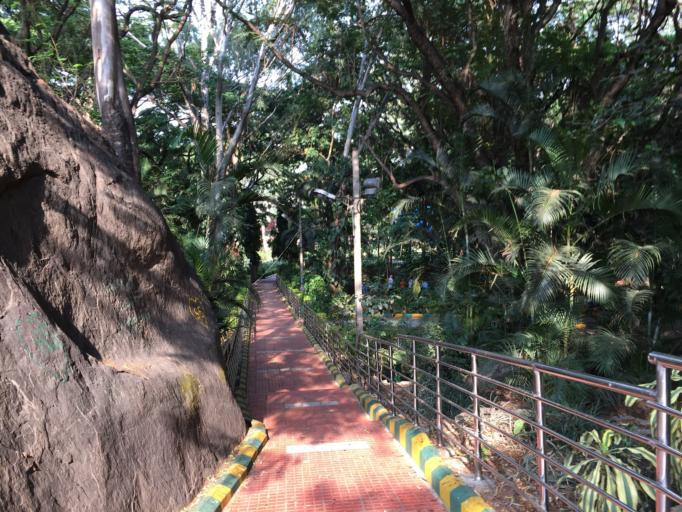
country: IN
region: Karnataka
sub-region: Bangalore Urban
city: Bangalore
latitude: 12.9430
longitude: 77.5691
